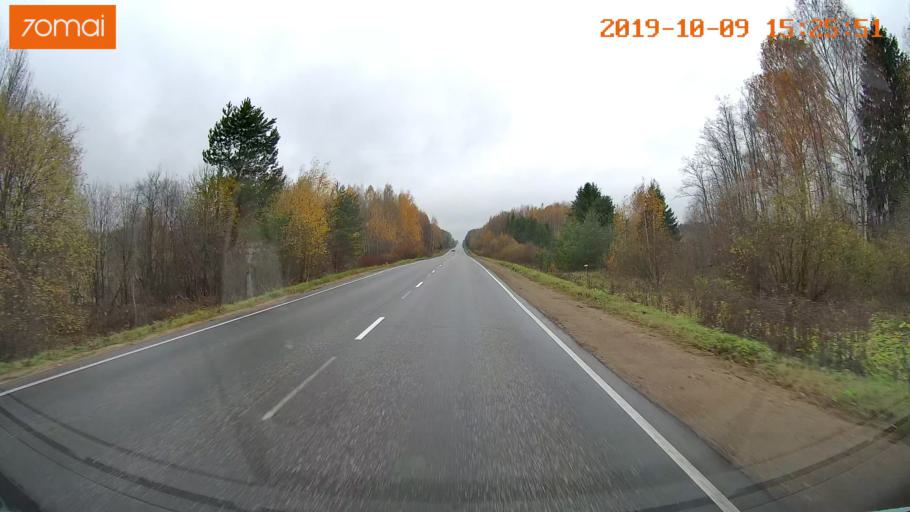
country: RU
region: Kostroma
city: Susanino
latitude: 58.0241
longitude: 41.4184
